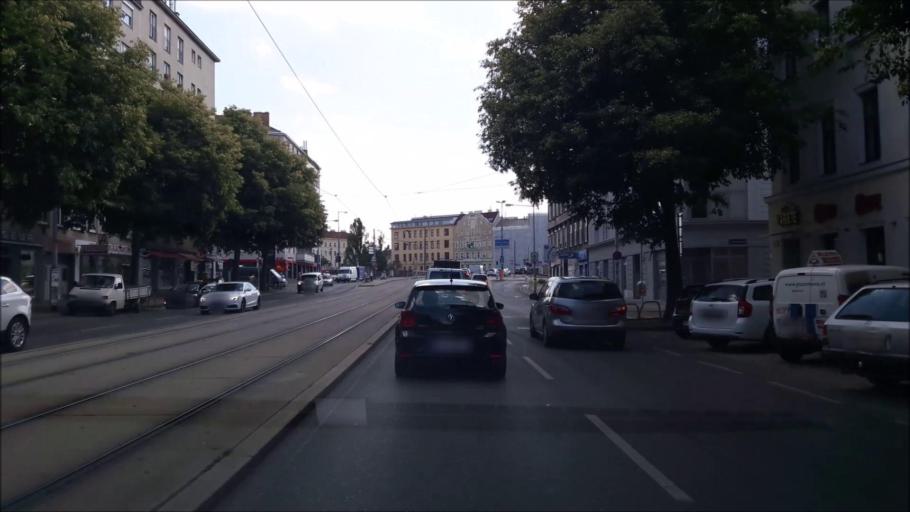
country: AT
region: Vienna
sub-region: Wien Stadt
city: Vienna
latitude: 48.2148
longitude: 16.3912
